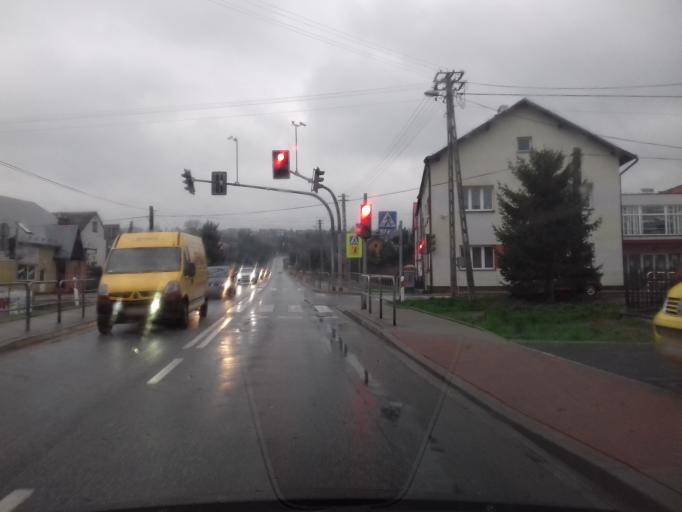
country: PL
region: Lesser Poland Voivodeship
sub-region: Powiat nowosadecki
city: Chelmiec
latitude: 49.6310
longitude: 20.6491
